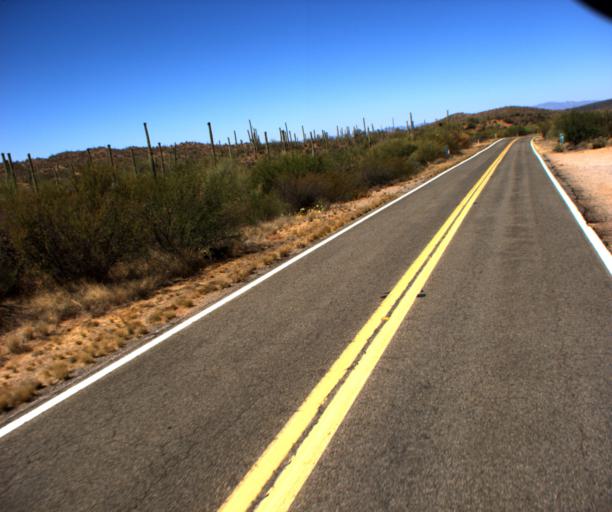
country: US
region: Arizona
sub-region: Pima County
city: Sells
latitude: 32.1759
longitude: -112.1948
